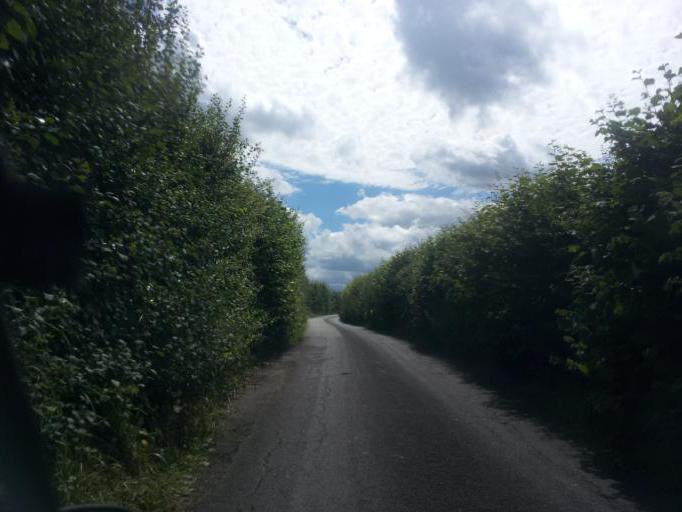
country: GB
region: England
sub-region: Kent
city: Kings Hill
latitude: 51.2702
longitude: 0.3839
